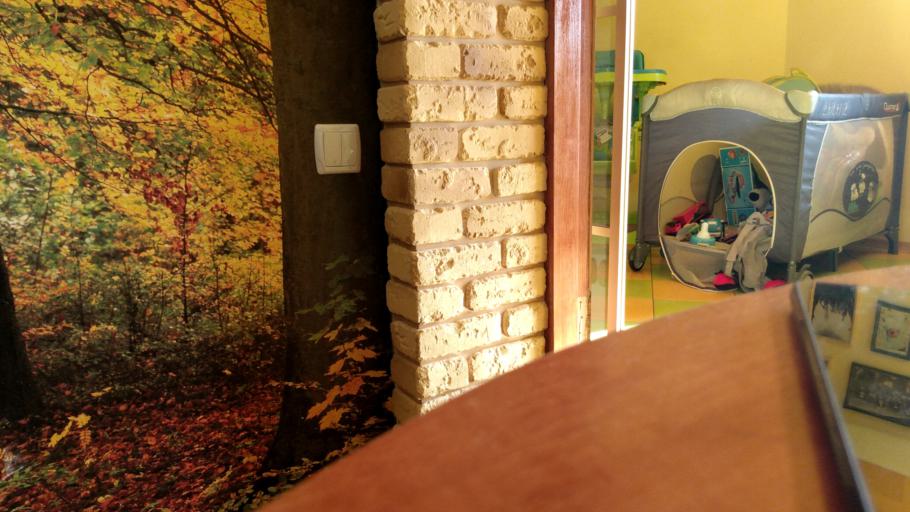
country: RU
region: Tverskaya
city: Novozavidovskiy
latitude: 56.6569
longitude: 36.4982
